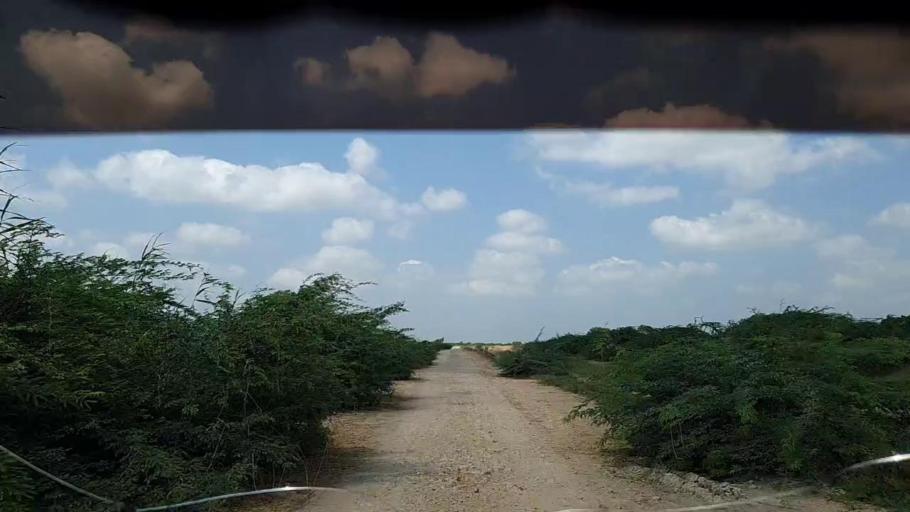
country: PK
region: Sindh
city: Kadhan
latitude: 24.5936
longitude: 68.9650
